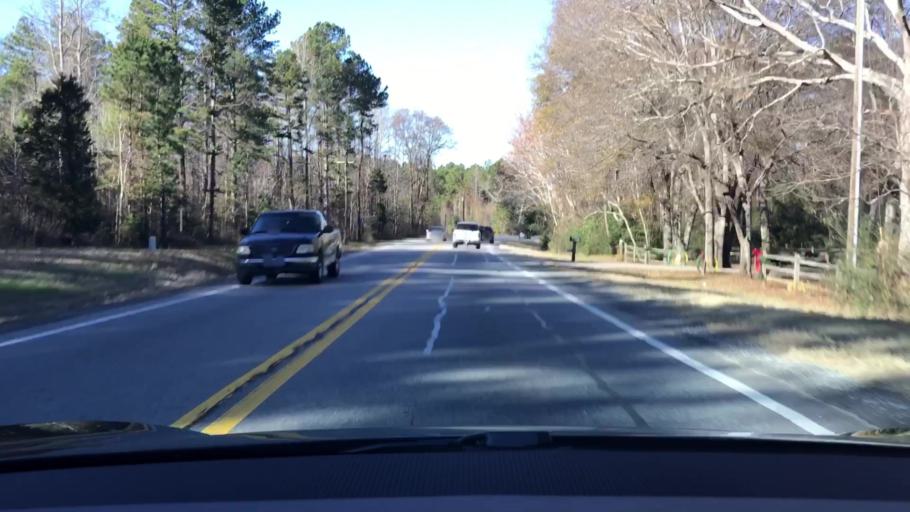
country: US
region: Georgia
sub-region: Walton County
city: Monroe
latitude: 33.8742
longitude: -83.7203
